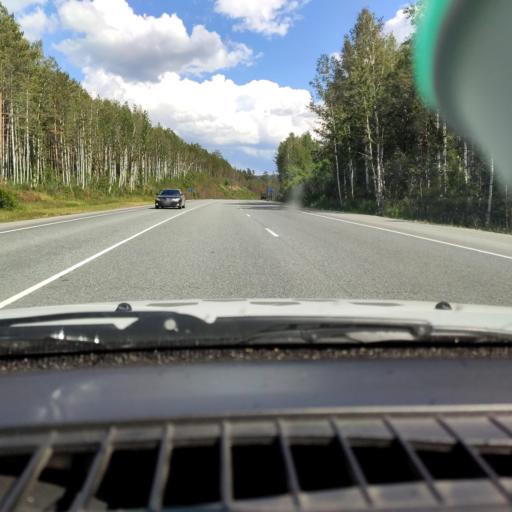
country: RU
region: Chelyabinsk
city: Zlatoust
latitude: 55.0541
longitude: 59.7125
